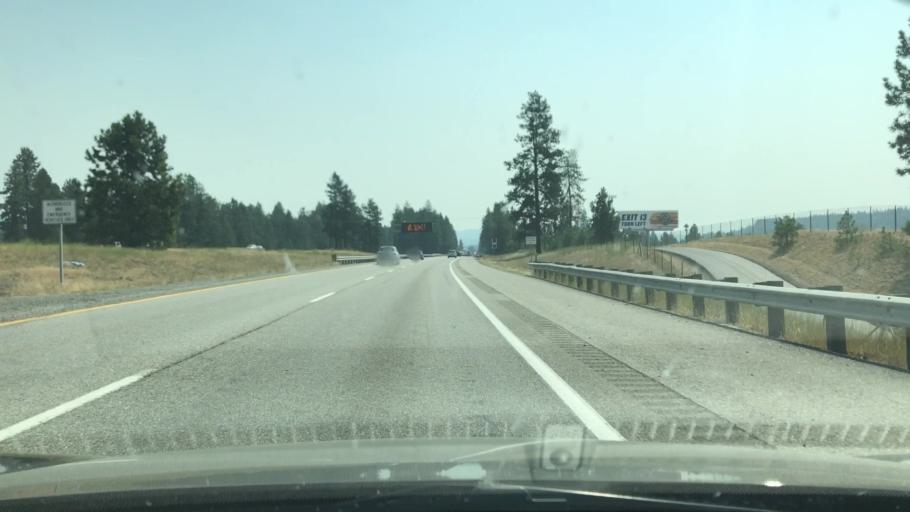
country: US
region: Idaho
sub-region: Kootenai County
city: Coeur d'Alene
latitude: 47.7079
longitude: -116.8541
